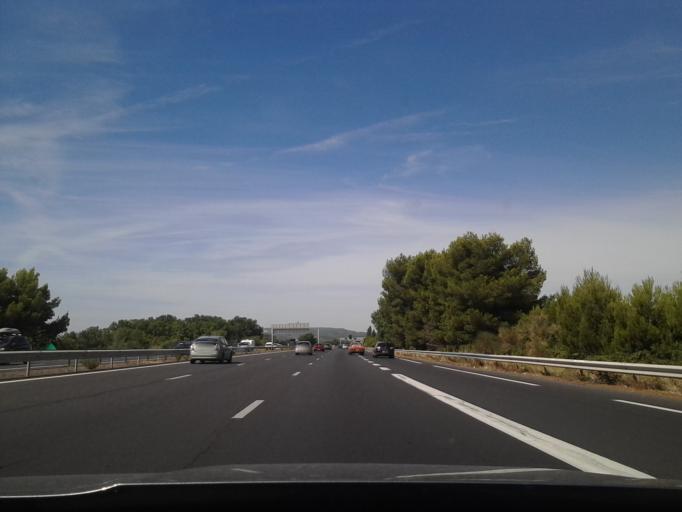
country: FR
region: Languedoc-Roussillon
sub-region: Departement de l'Aude
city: Narbonne
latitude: 43.1758
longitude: 3.0322
